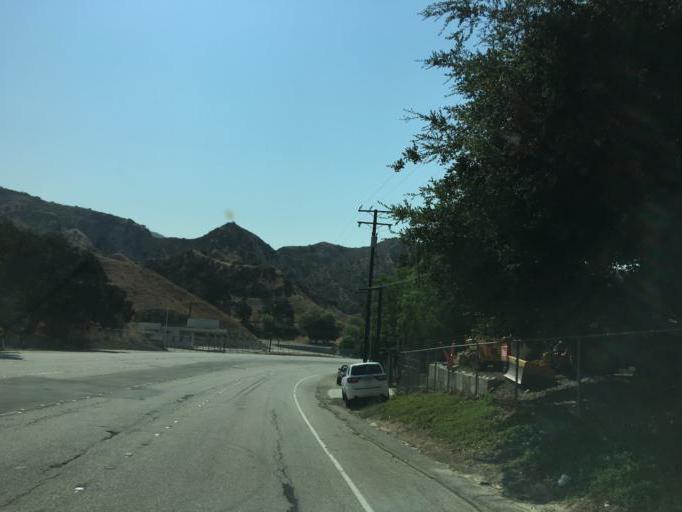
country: US
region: California
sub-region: Los Angeles County
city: Santa Clarita
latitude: 34.3382
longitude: -118.5056
